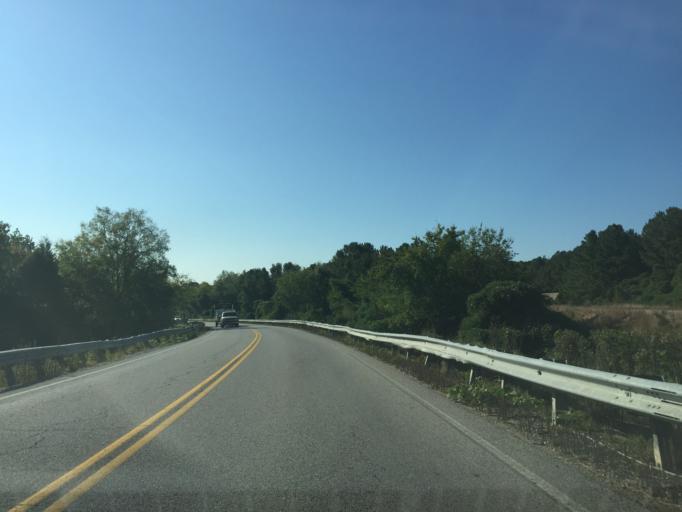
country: US
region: Tennessee
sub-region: Hamilton County
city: Harrison
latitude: 35.0877
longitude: -85.1619
